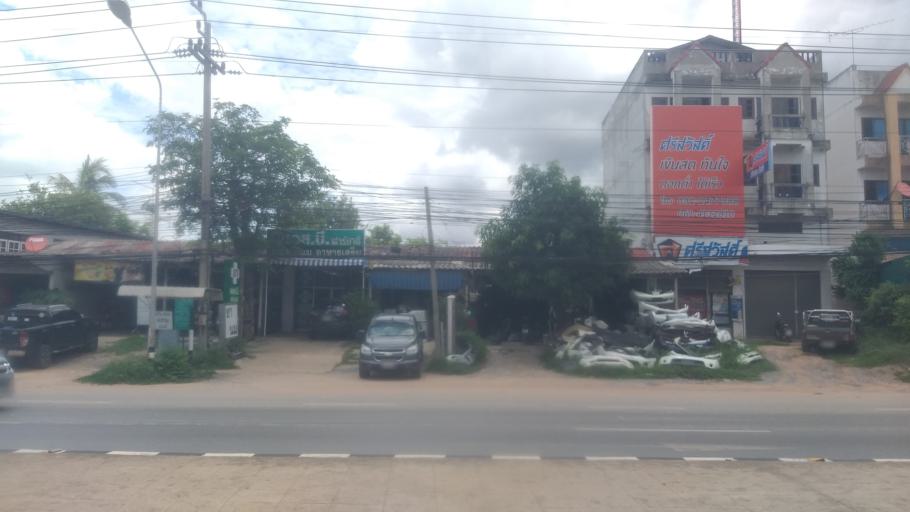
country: TH
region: Nakhon Ratchasima
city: Nakhon Ratchasima
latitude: 15.0797
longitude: 102.1151
